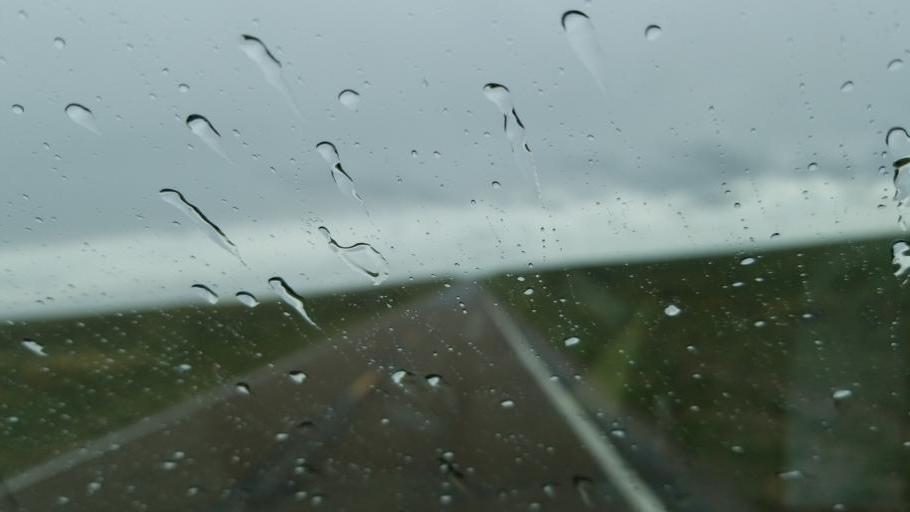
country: US
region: Colorado
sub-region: Lincoln County
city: Hugo
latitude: 38.8494
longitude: -103.2629
